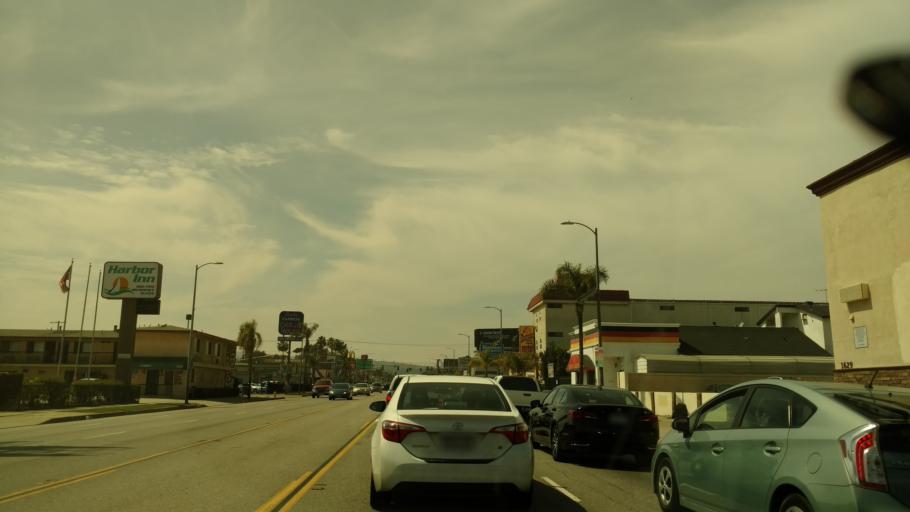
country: US
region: California
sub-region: Los Angeles County
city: Lomita
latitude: 33.7895
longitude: -118.3051
